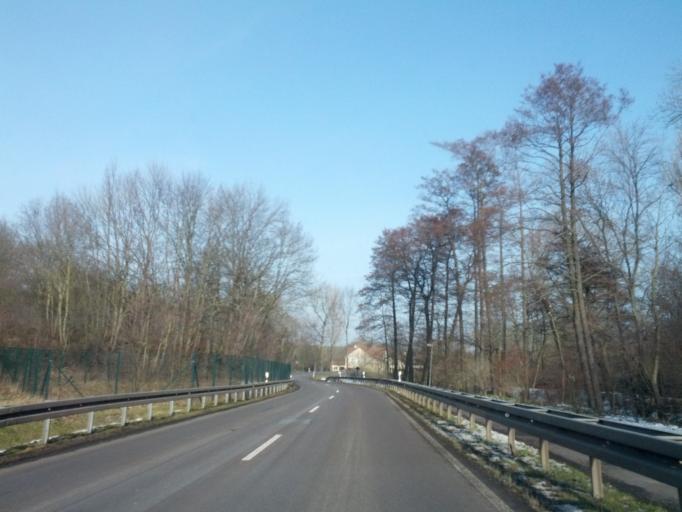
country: DE
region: Thuringia
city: Neudietendorf
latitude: 50.9178
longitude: 10.9222
